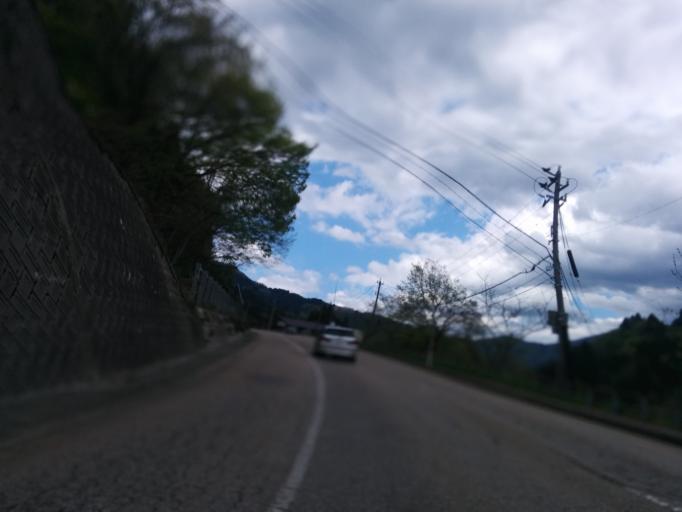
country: JP
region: Toyama
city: Nanto-shi
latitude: 36.4232
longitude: 136.9385
